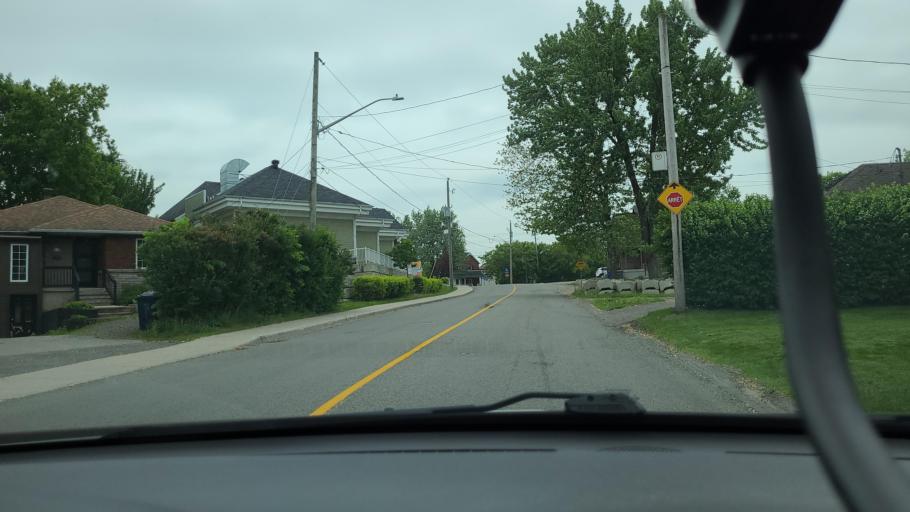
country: CA
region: Quebec
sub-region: Laurentides
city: Rosemere
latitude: 45.6248
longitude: -73.7751
